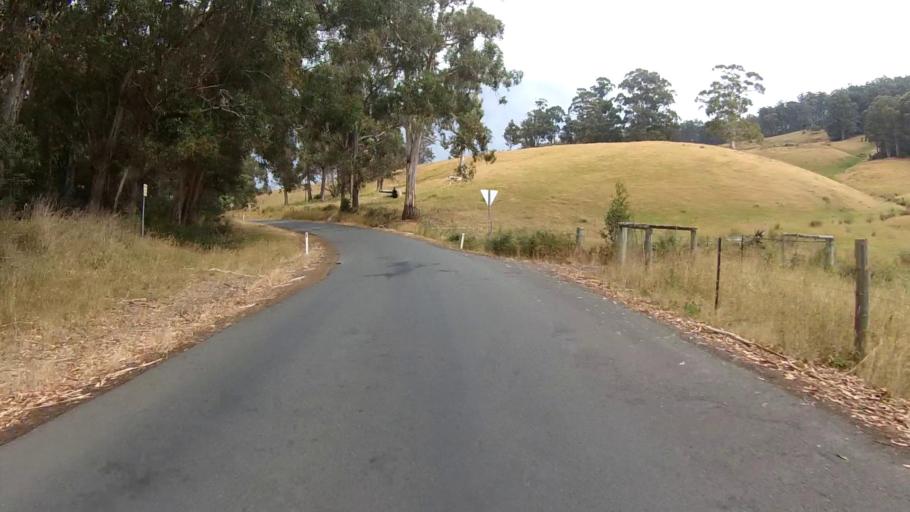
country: AU
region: Tasmania
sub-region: Huon Valley
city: Cygnet
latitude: -43.1811
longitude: 147.1139
